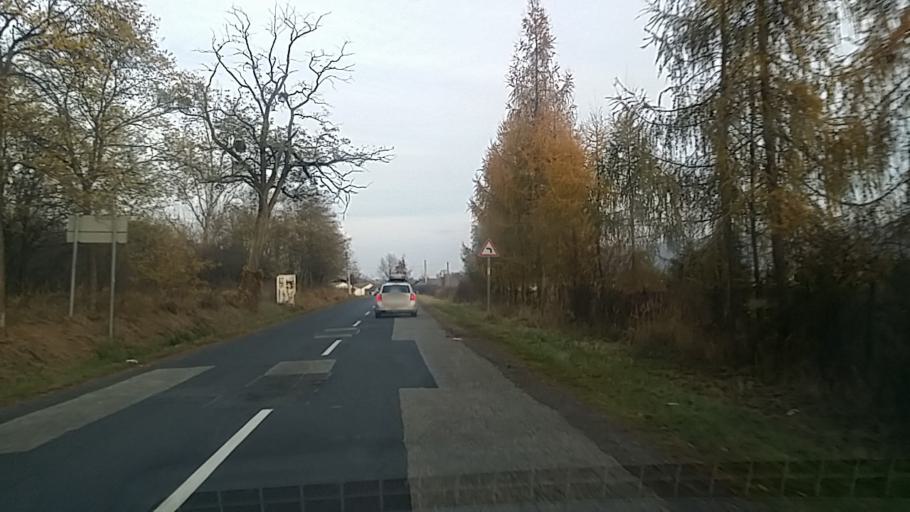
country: HU
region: Borsod-Abauj-Zemplen
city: Sarospatak
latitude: 48.4695
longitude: 21.5012
